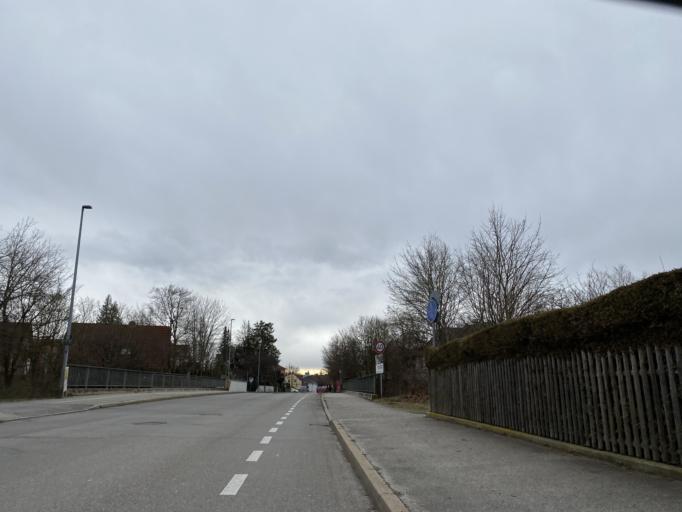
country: DE
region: Bavaria
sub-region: Upper Bavaria
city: Fuerstenfeldbruck
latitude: 48.1888
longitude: 11.2556
